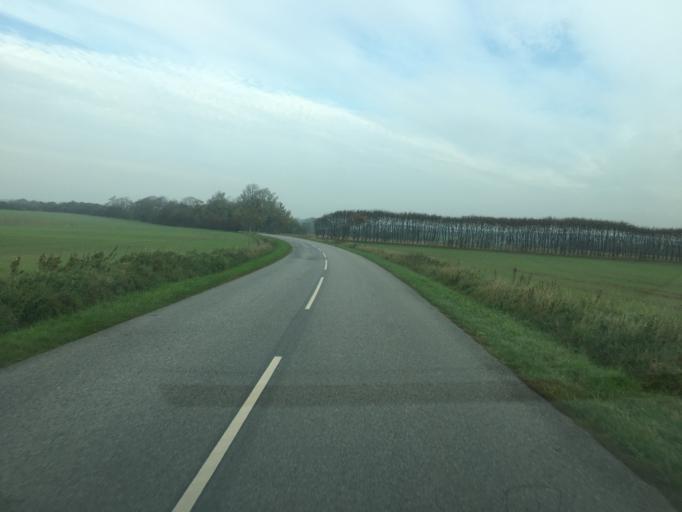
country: DK
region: South Denmark
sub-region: Tonder Kommune
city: Toftlund
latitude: 55.1084
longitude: 9.0887
